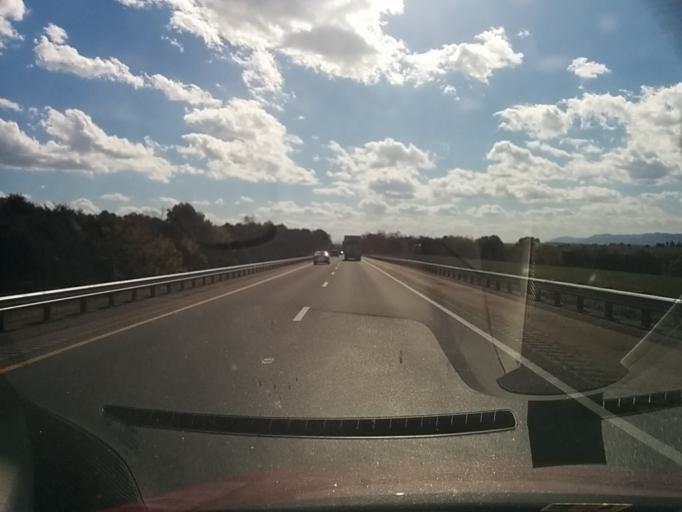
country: US
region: Virginia
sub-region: Rockbridge County
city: East Lexington
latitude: 37.8127
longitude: -79.3860
